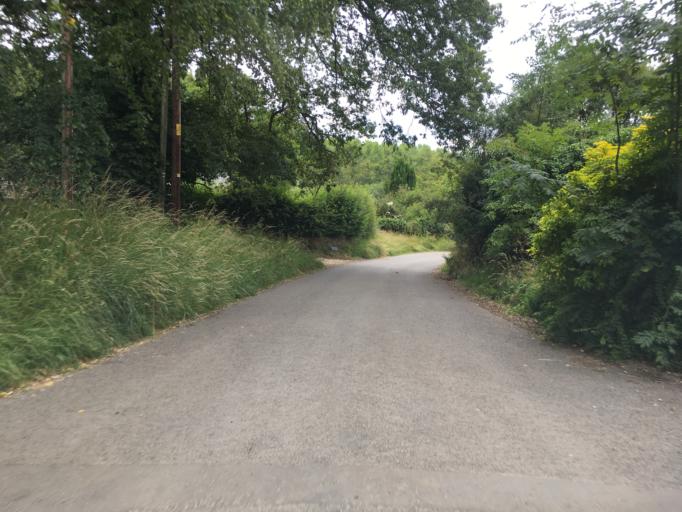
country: GB
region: England
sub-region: Oxfordshire
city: Charlbury
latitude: 51.9011
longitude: -1.5019
